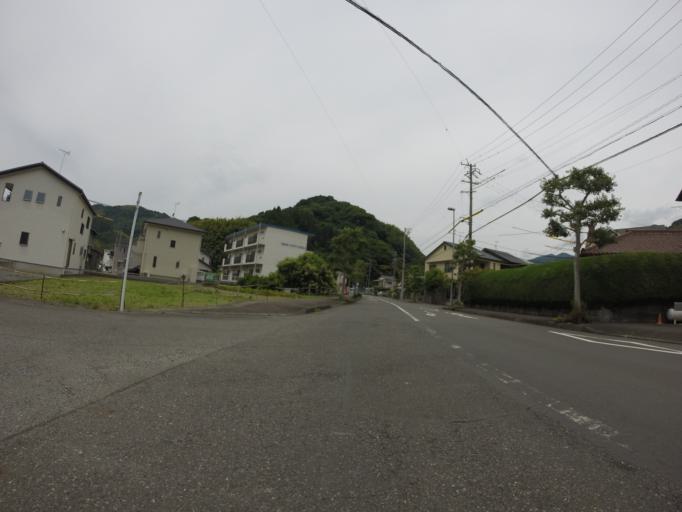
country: JP
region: Shizuoka
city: Shizuoka-shi
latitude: 35.0345
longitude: 138.4265
